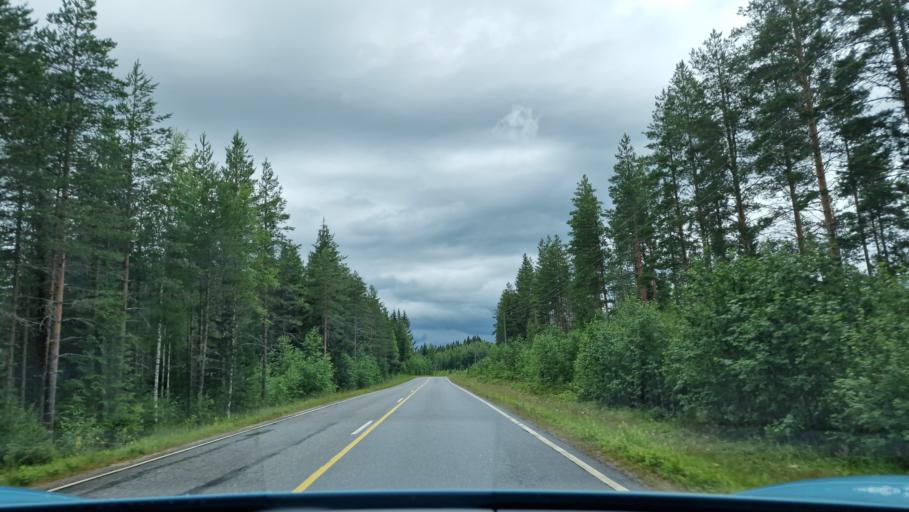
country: FI
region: Southern Ostrobothnia
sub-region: Jaerviseutu
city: Soini
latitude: 62.7239
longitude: 24.4242
